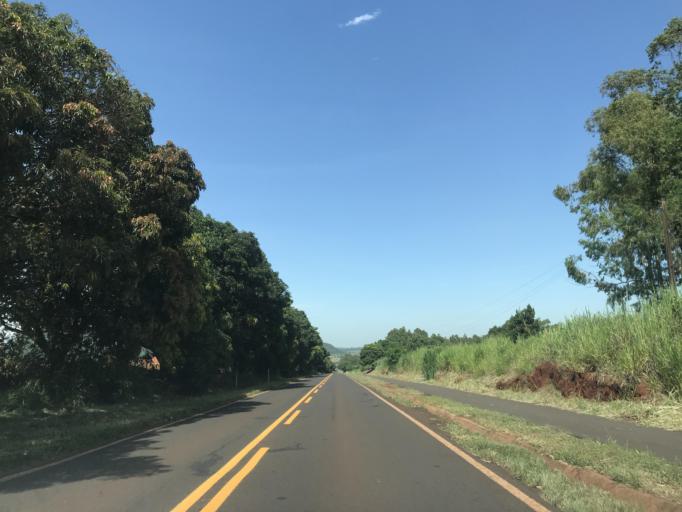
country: BR
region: Parana
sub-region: Terra Rica
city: Terra Rica
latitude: -22.7543
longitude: -52.6276
